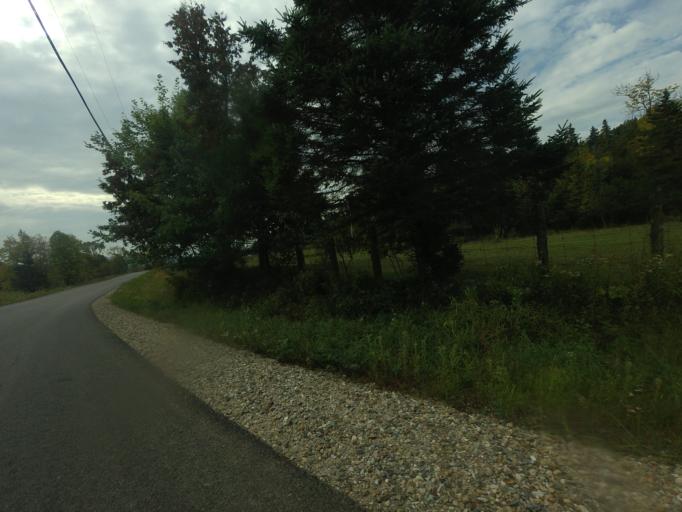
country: CA
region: Quebec
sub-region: Outaouais
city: Wakefield
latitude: 45.9856
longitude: -75.9408
